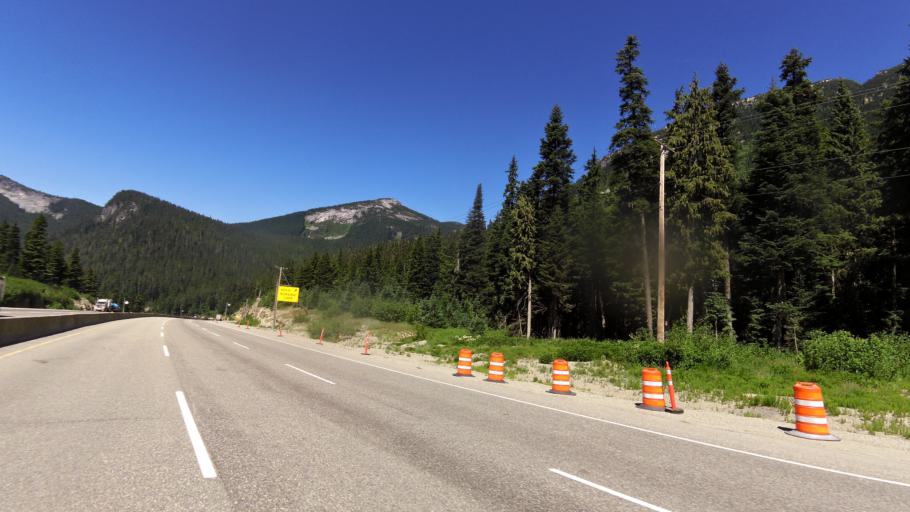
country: CA
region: British Columbia
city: Hope
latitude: 49.5963
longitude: -121.1276
